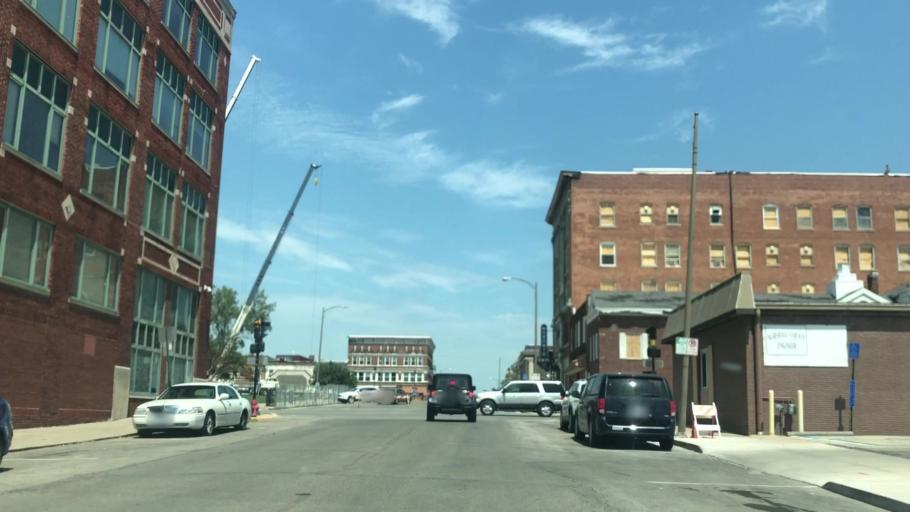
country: US
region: Iowa
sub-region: Marshall County
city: Marshalltown
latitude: 42.0475
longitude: -92.9113
